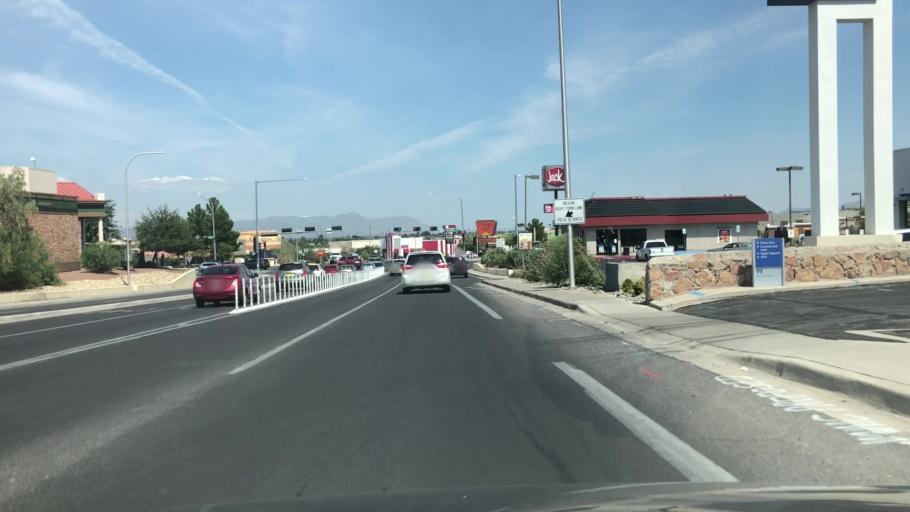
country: US
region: New Mexico
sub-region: Dona Ana County
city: University Park
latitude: 32.3145
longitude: -106.7436
